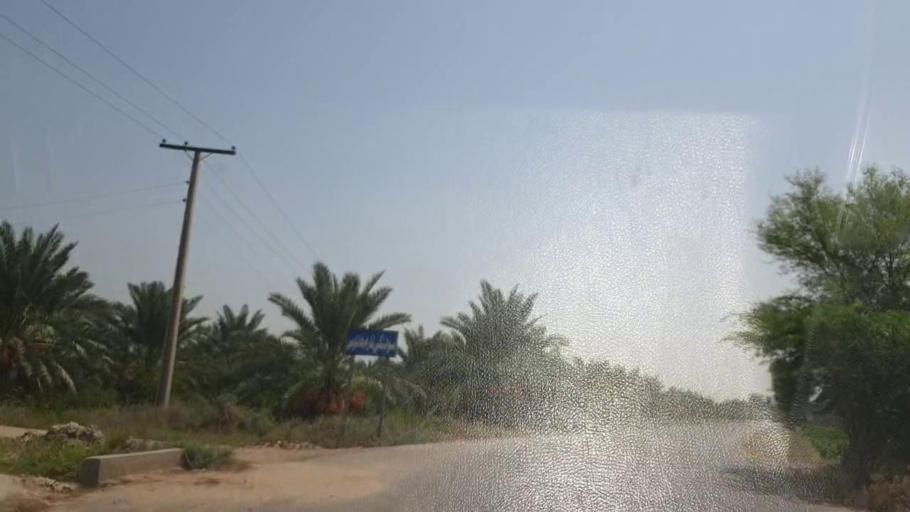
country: PK
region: Sindh
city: Bozdar
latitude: 27.2835
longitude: 68.6257
